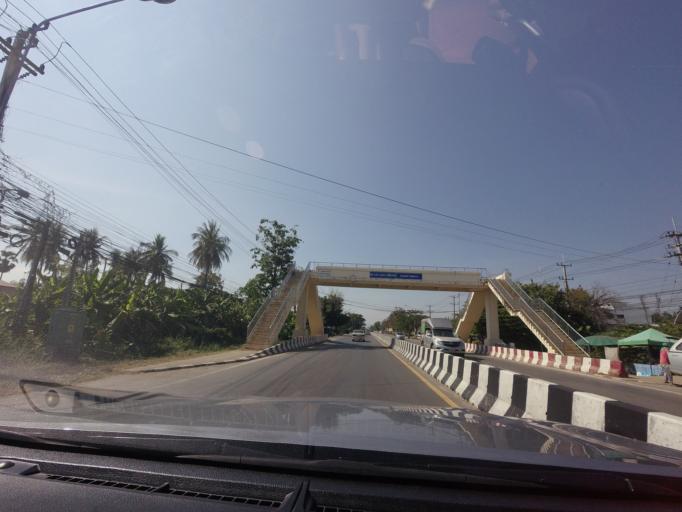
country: TH
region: Sukhothai
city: Sukhothai
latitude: 17.0103
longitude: 99.7913
